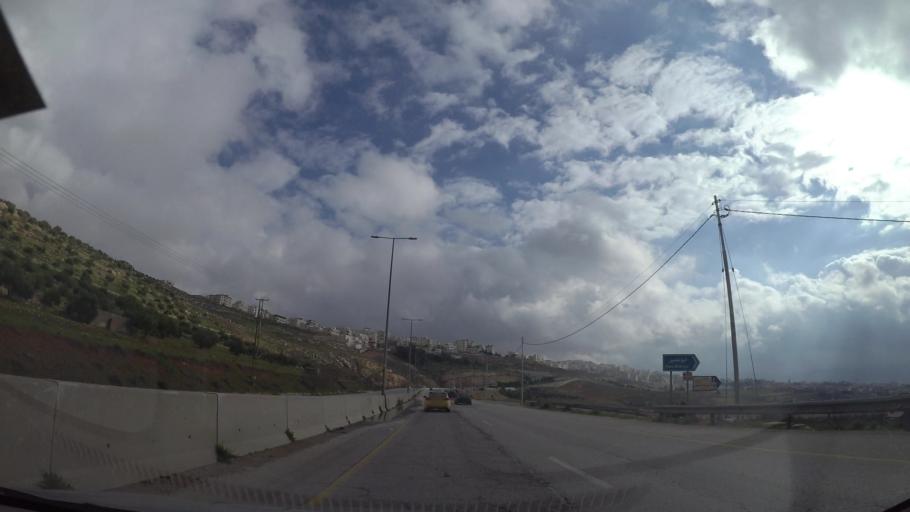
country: JO
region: Amman
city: Al Jubayhah
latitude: 32.0776
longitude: 35.8786
